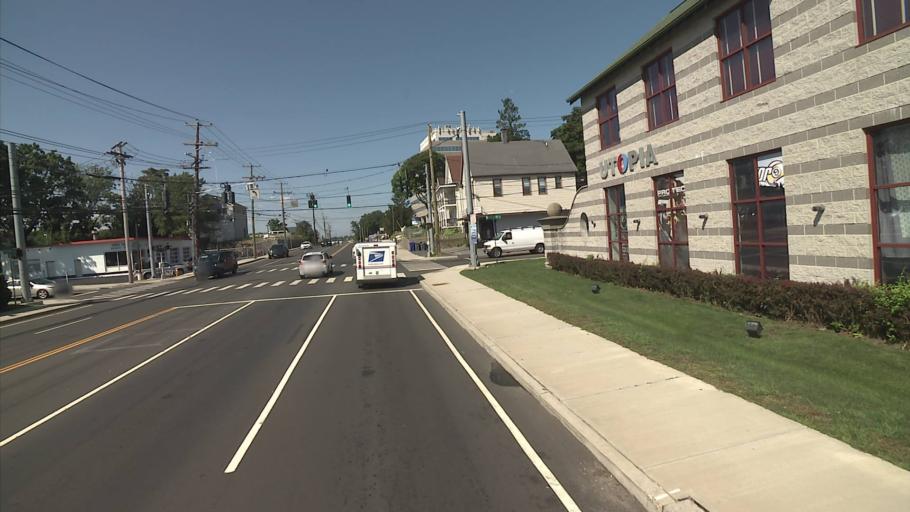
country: US
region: Connecticut
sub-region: Fairfield County
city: Norwalk
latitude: 41.1049
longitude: -73.4301
